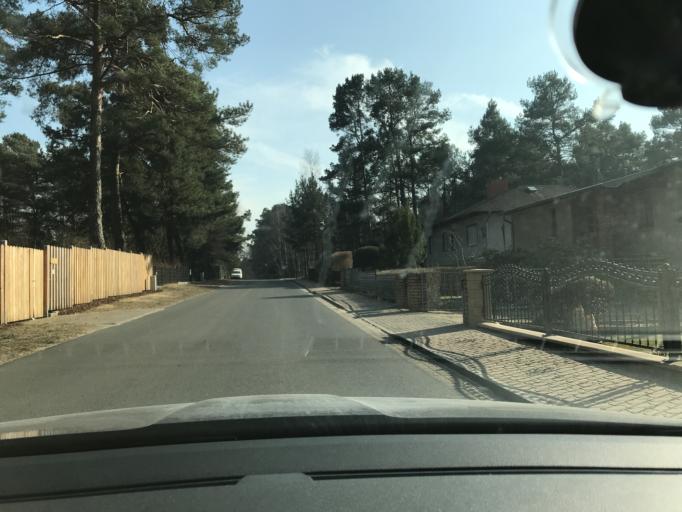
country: DE
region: Brandenburg
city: Munchehofe
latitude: 52.2157
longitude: 13.7817
